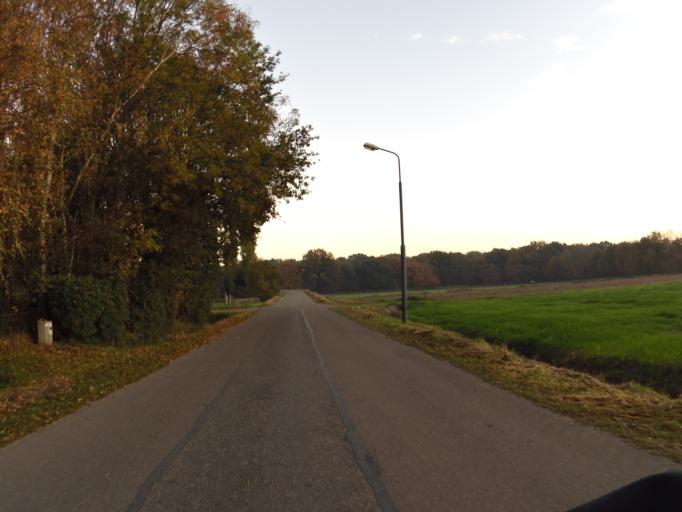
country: NL
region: North Brabant
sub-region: Gemeente Vught
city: Vught
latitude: 51.6731
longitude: 5.2811
